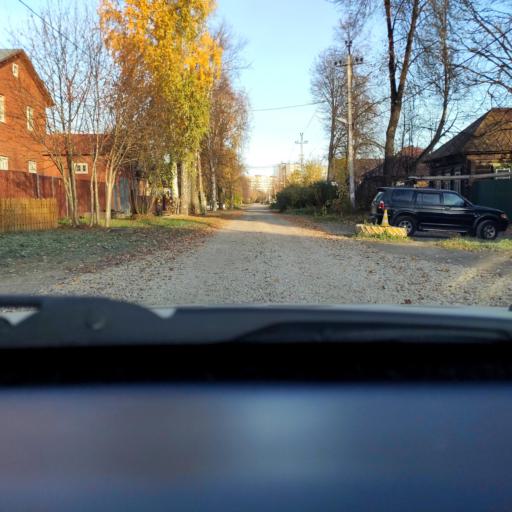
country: RU
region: Perm
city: Perm
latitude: 58.0247
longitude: 56.3282
